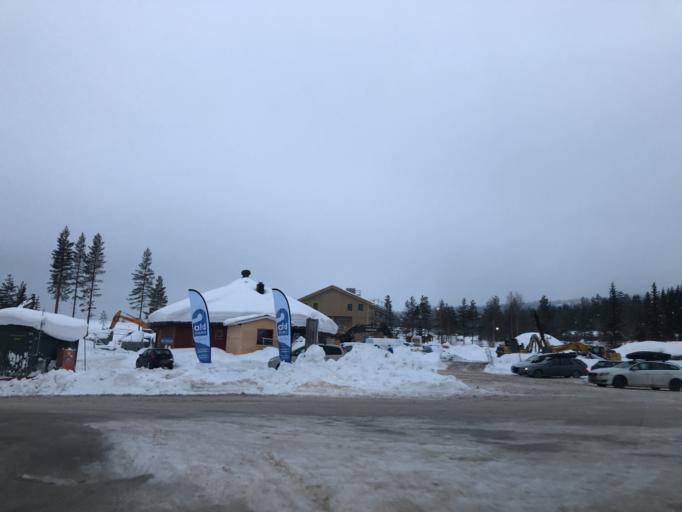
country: NO
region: Hedmark
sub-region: Trysil
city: Innbygda
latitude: 61.3059
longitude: 12.2443
